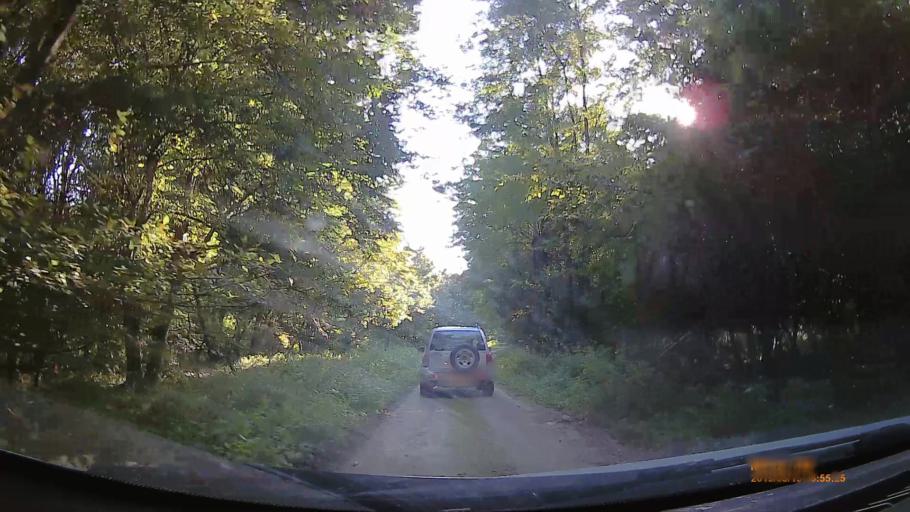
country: HU
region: Zala
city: Pacsa
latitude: 46.6000
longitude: 17.0565
